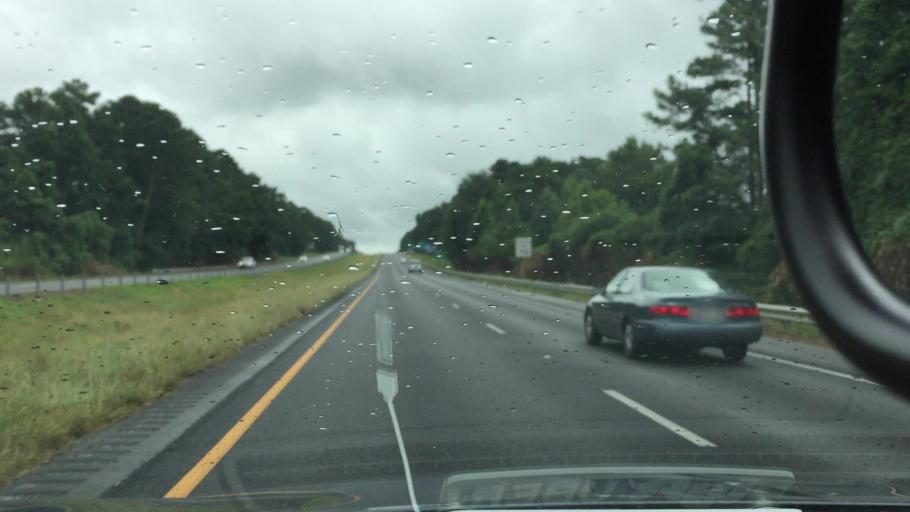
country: US
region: Alabama
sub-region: Lee County
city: Opelika
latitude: 32.6096
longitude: -85.4176
